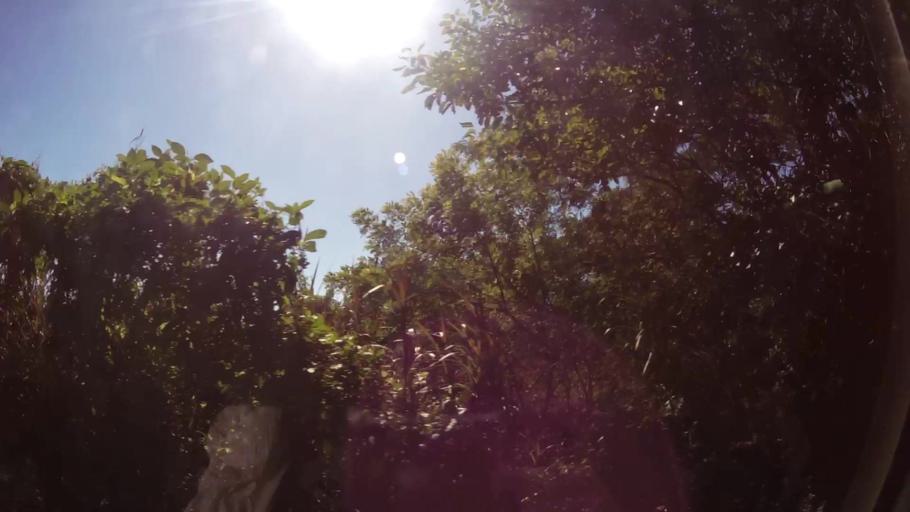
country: GT
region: Escuintla
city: Iztapa
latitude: 13.9239
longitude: -90.5904
